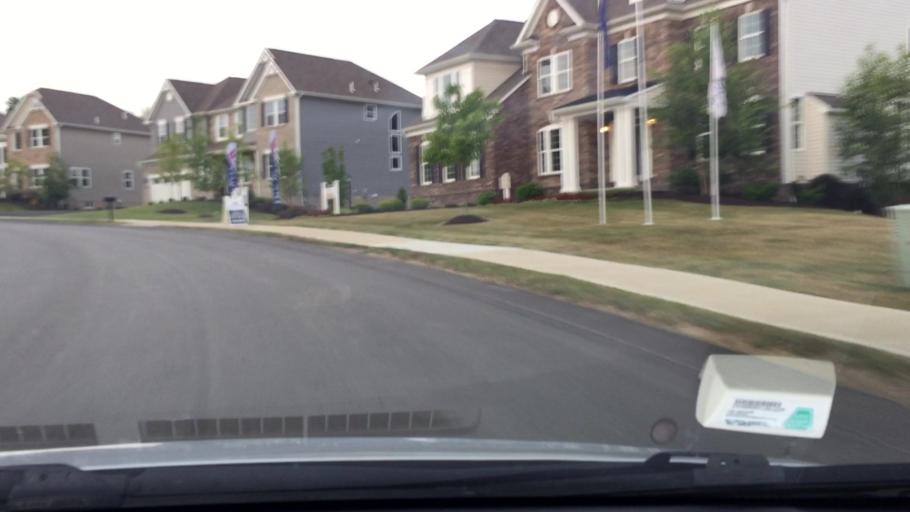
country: US
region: Pennsylvania
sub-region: Allegheny County
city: Gibsonia
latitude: 40.6363
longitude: -80.0245
